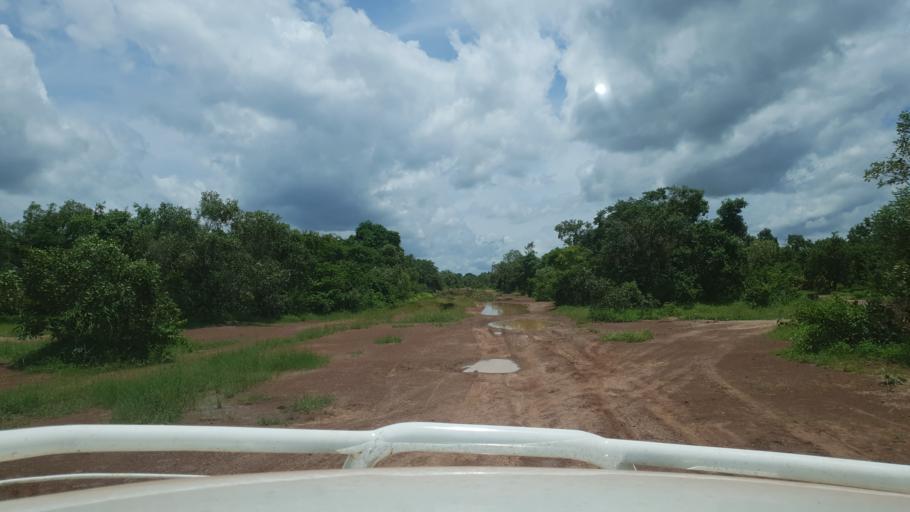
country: ML
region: Koulikoro
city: Banamba
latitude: 13.1980
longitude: -7.3272
